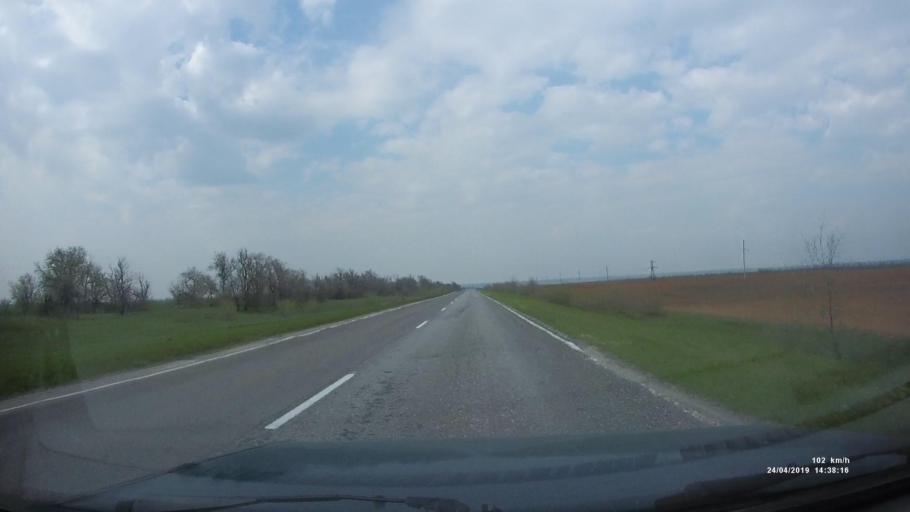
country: RU
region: Rostov
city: Remontnoye
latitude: 46.3987
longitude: 43.8861
